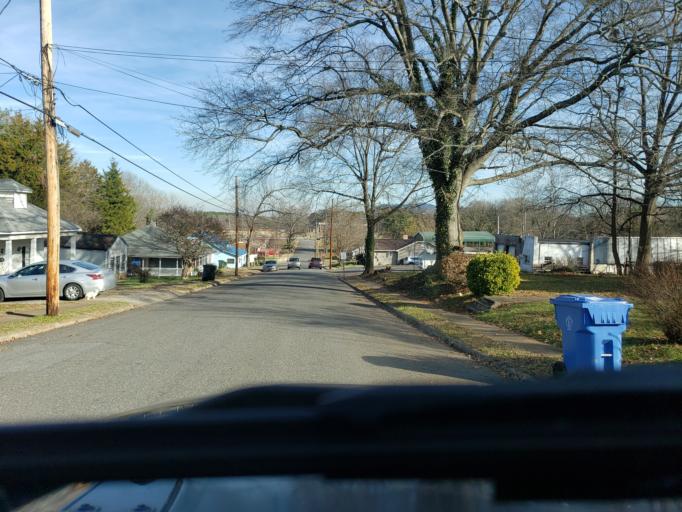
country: US
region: North Carolina
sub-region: Cleveland County
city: Kings Mountain
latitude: 35.2441
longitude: -81.3376
